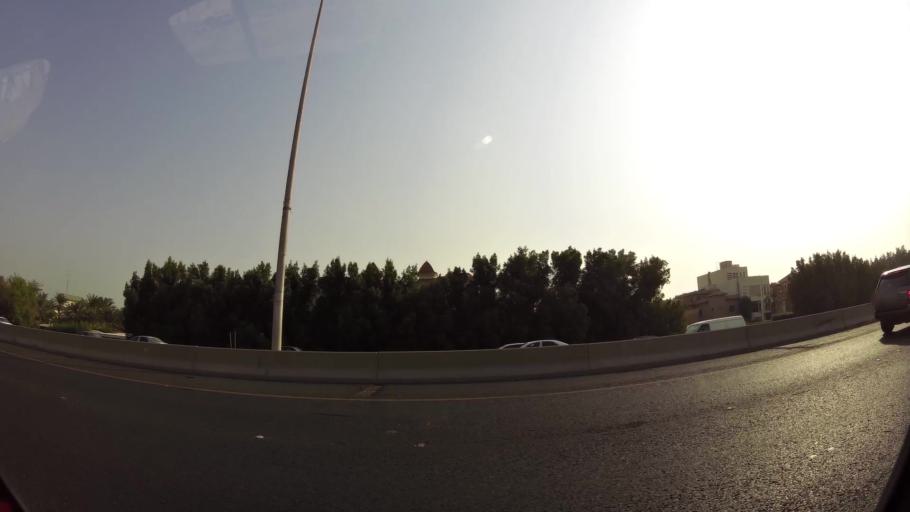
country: KW
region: Mubarak al Kabir
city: Mubarak al Kabir
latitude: 29.2002
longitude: 48.1069
